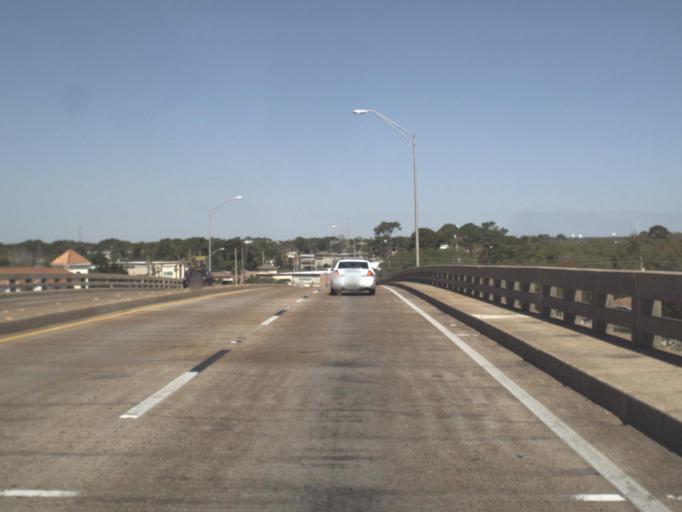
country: US
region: Florida
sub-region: Okaloosa County
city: Fort Walton Beach
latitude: 30.4011
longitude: -86.6005
